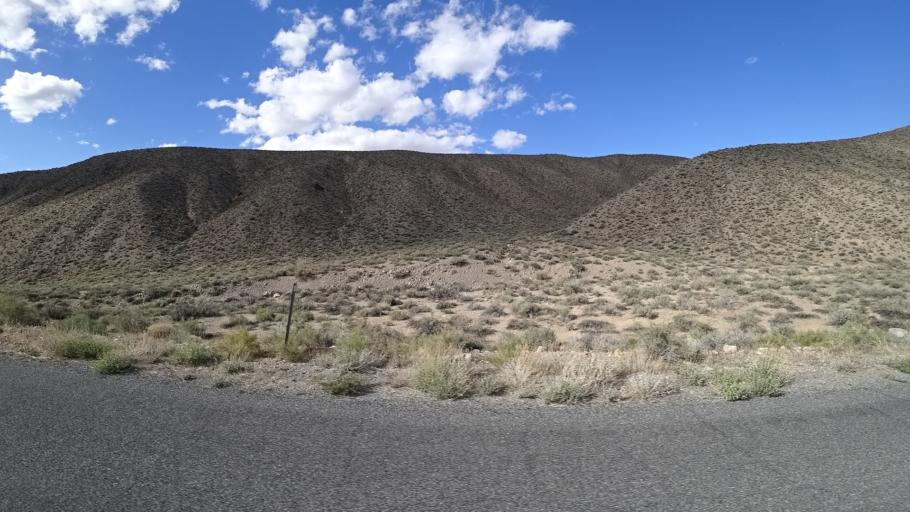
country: US
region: Nevada
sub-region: Nye County
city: Beatty
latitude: 36.3953
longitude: -117.1580
